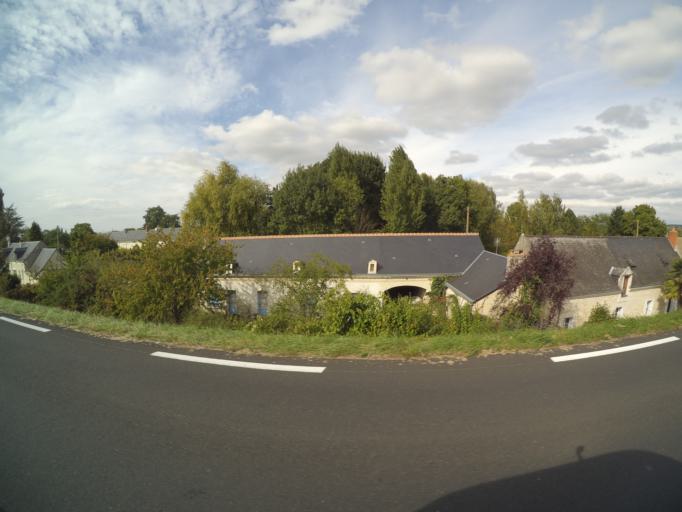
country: FR
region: Centre
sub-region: Departement d'Indre-et-Loire
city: Huismes
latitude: 47.2600
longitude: 0.2593
